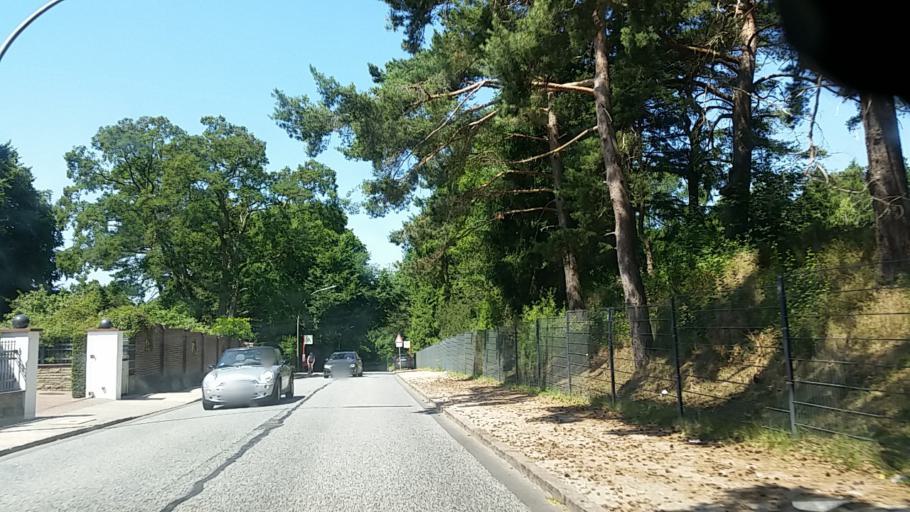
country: DE
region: Schleswig-Holstein
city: Wedel
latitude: 53.5658
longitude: 9.7848
